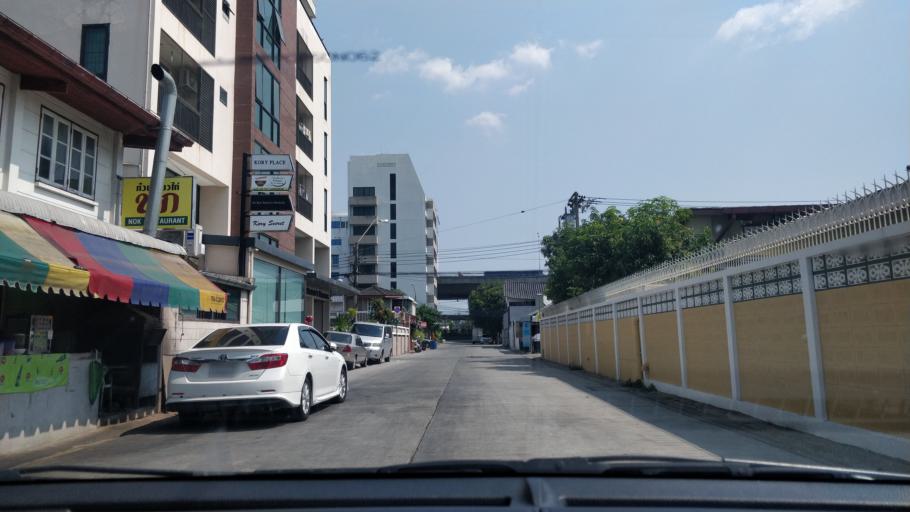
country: TH
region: Bangkok
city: Suan Luang
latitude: 13.7440
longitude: 100.6331
